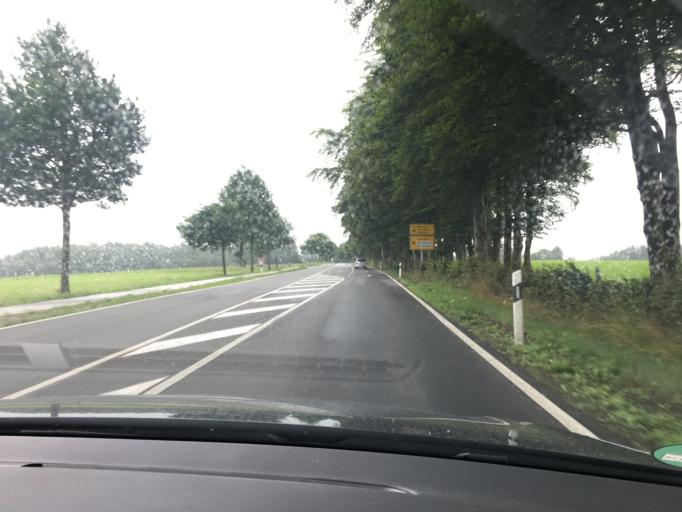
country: DE
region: North Rhine-Westphalia
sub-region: Regierungsbezirk Koln
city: Hurtgenwald
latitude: 50.6799
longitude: 6.3464
